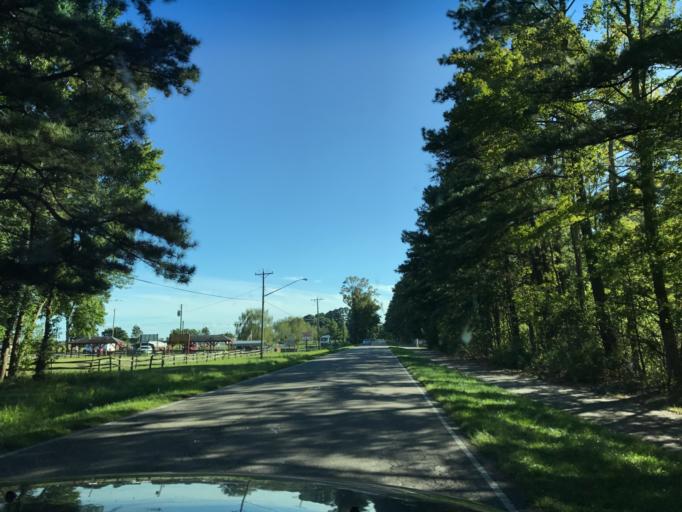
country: US
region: Virginia
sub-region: City of Portsmouth
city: Portsmouth Heights
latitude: 36.7146
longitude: -76.3522
